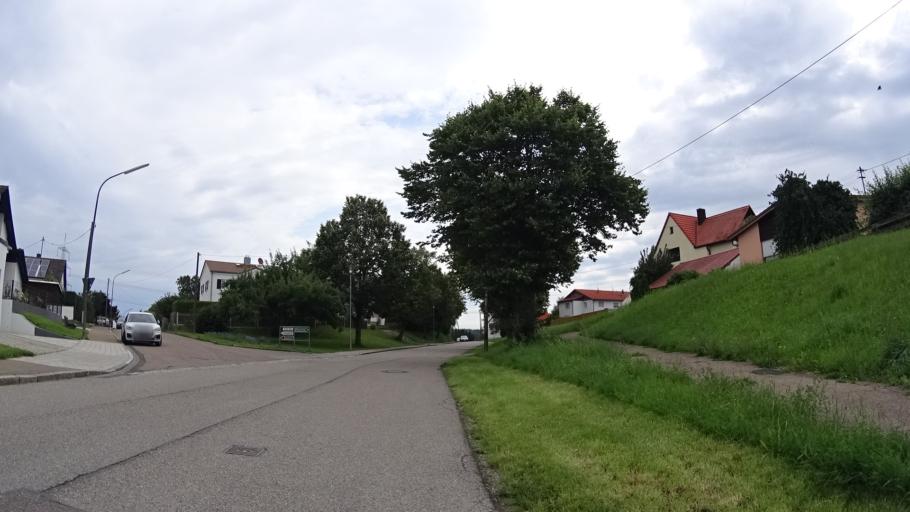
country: DE
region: Bavaria
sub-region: Upper Bavaria
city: Wettstetten
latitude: 48.8259
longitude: 11.4177
